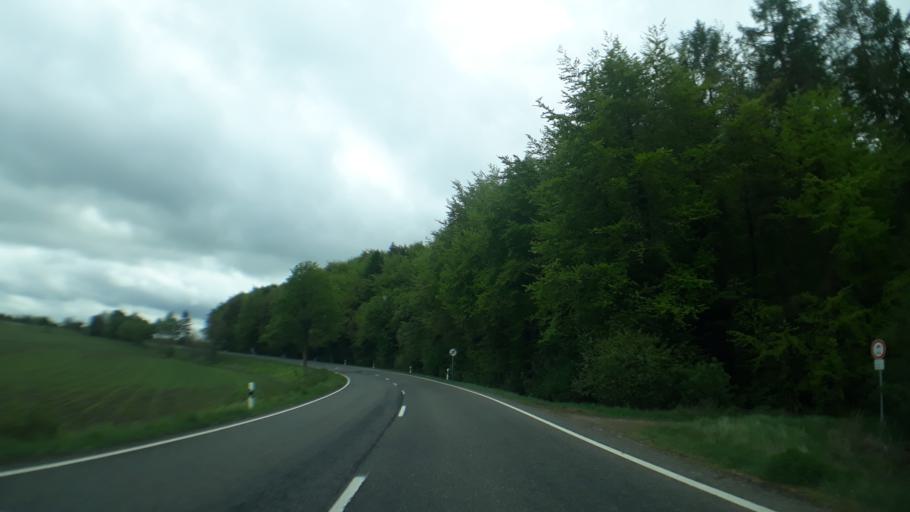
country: DE
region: North Rhine-Westphalia
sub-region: Regierungsbezirk Koln
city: Kall
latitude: 50.5240
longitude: 6.5866
